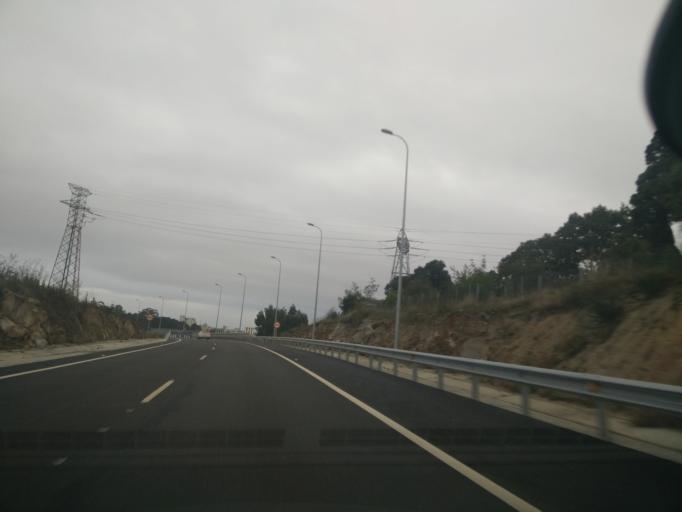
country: ES
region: Galicia
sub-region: Provincia da Coruna
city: A Coruna
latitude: 43.3337
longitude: -8.4209
